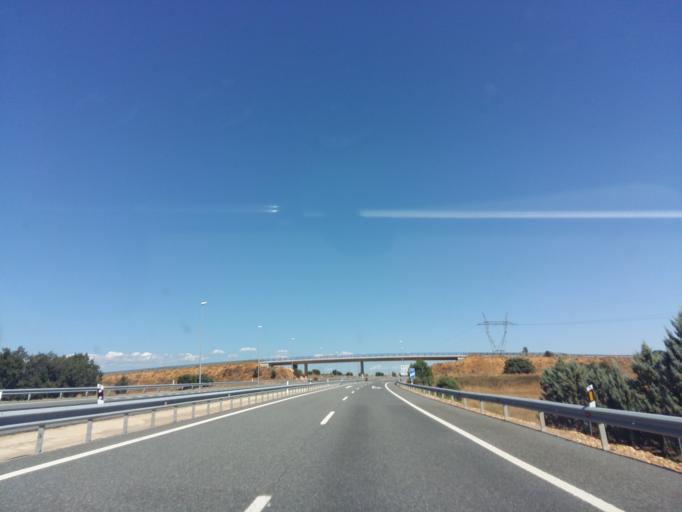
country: ES
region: Castille and Leon
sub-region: Provincia de Leon
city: Villadangos del Paramo
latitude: 42.5384
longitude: -5.7334
